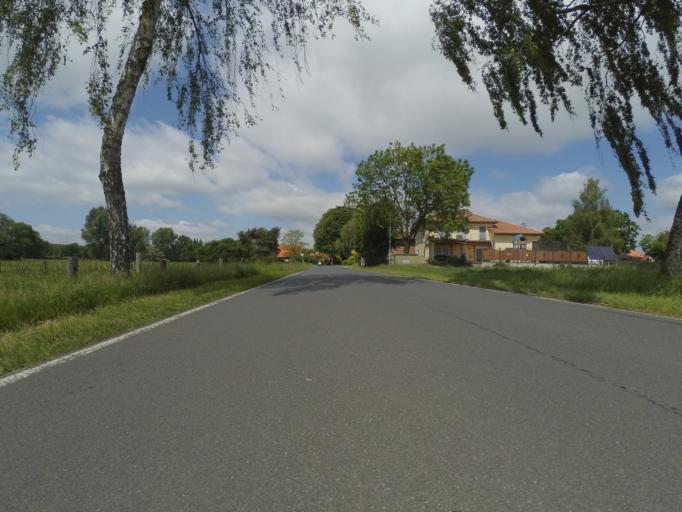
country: DE
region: Lower Saxony
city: Hillerse
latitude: 52.4087
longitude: 10.3364
